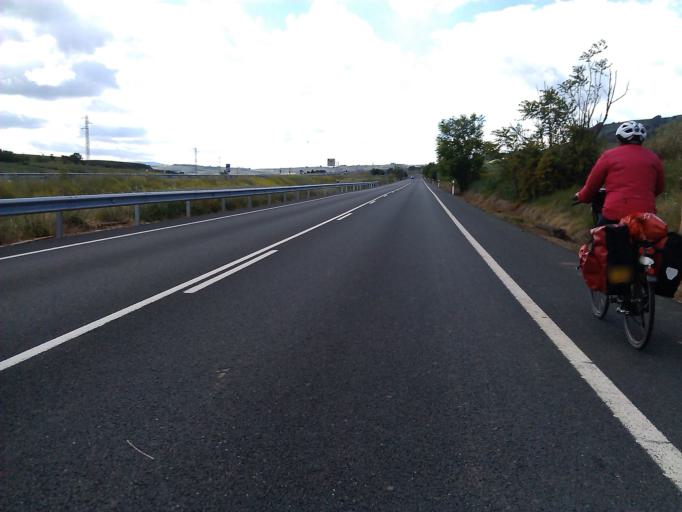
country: ES
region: La Rioja
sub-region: Provincia de La Rioja
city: Alesanco
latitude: 42.4345
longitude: -2.8249
